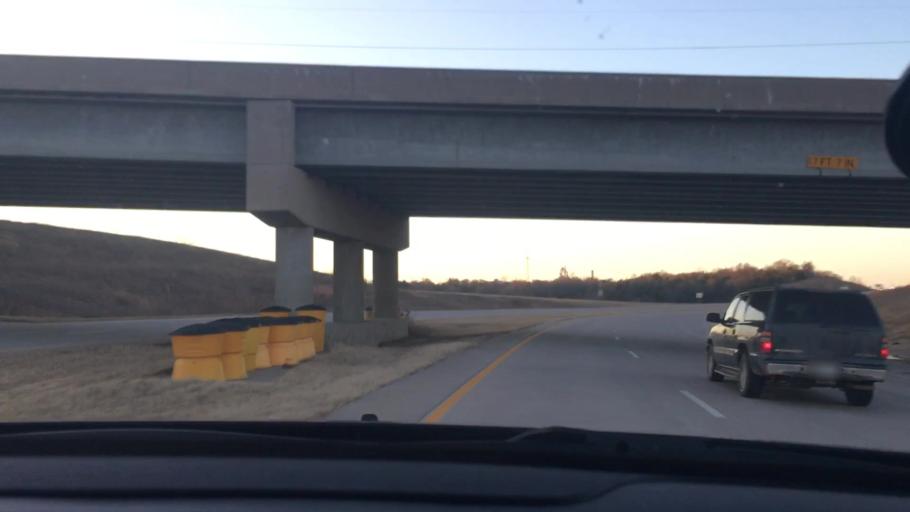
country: US
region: Oklahoma
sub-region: Pontotoc County
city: Ada
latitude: 34.7897
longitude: -96.6932
